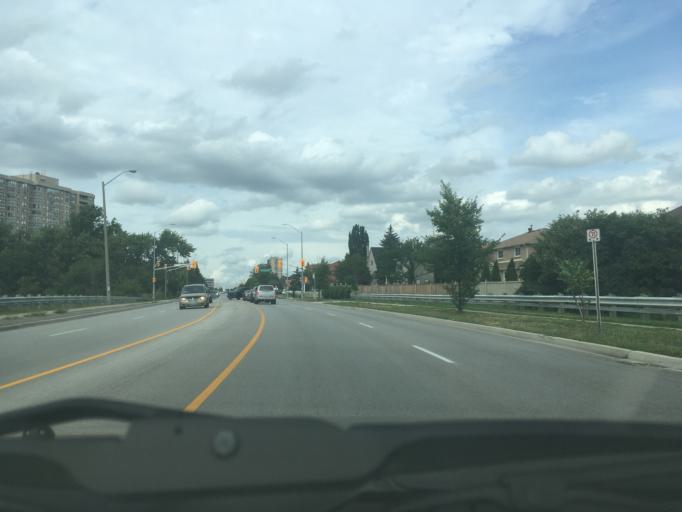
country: CA
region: Ontario
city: Brampton
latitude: 43.6540
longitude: -79.7285
